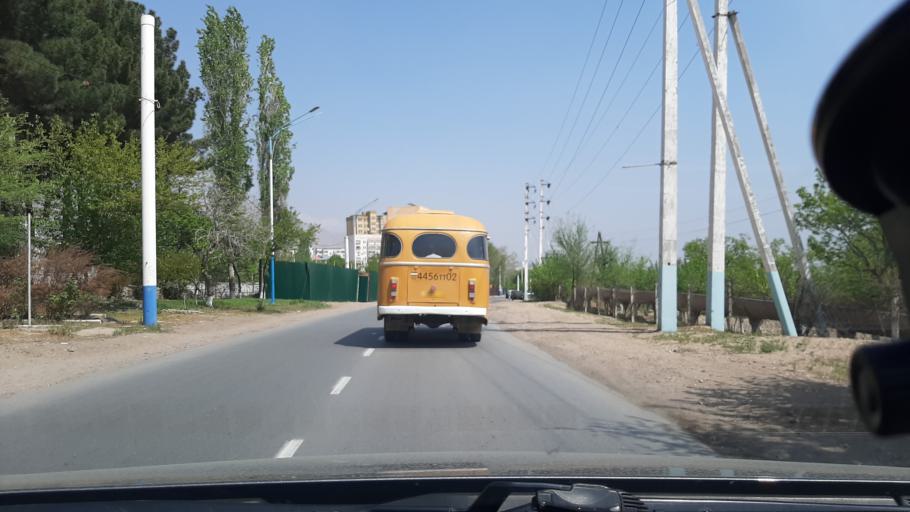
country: TJ
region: Viloyati Sughd
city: Khujand
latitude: 40.2863
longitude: 69.5909
